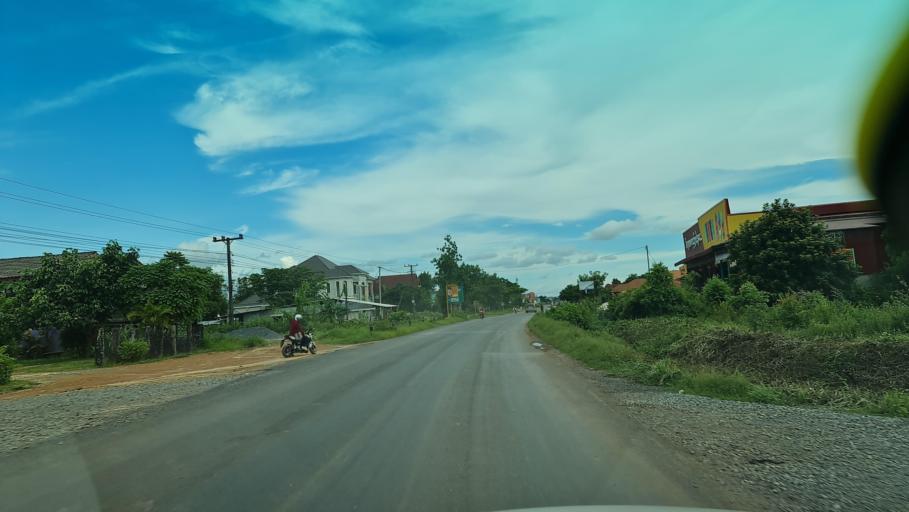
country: LA
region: Bolikhamxai
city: Ban Nahin
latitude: 18.1086
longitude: 104.2796
